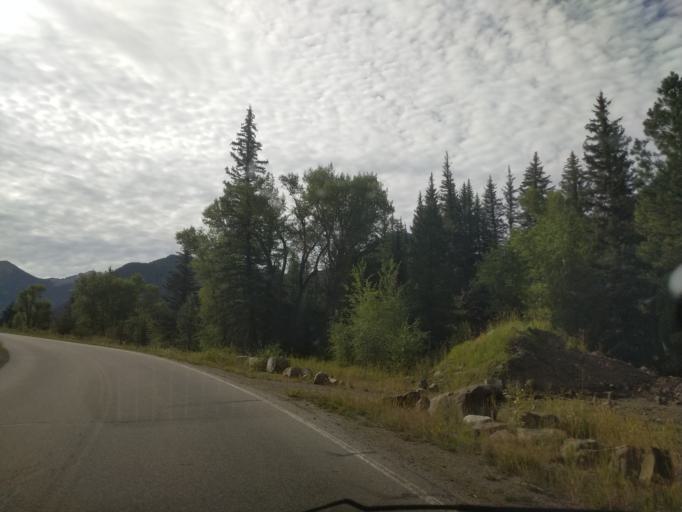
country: US
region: Colorado
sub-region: Pitkin County
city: Snowmass Village
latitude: 39.0807
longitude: -107.2314
